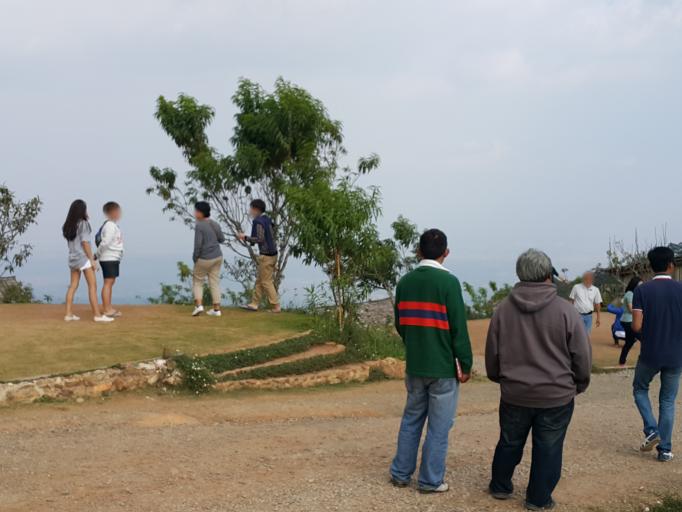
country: TH
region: Chiang Mai
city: Samoeng
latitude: 18.9359
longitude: 98.8223
